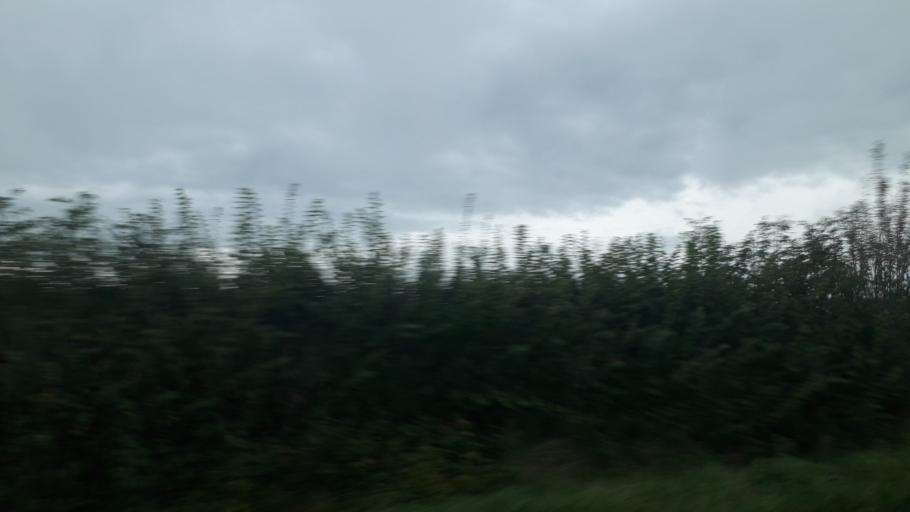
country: IE
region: Leinster
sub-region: An Longfort
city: Longford
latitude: 53.7254
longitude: -7.8653
